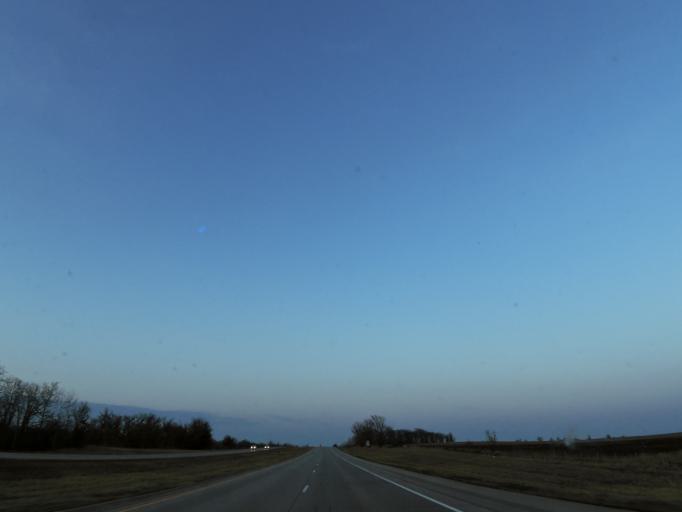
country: US
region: Minnesota
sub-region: Mower County
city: Grand Meadow
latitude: 43.6778
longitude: -92.7443
